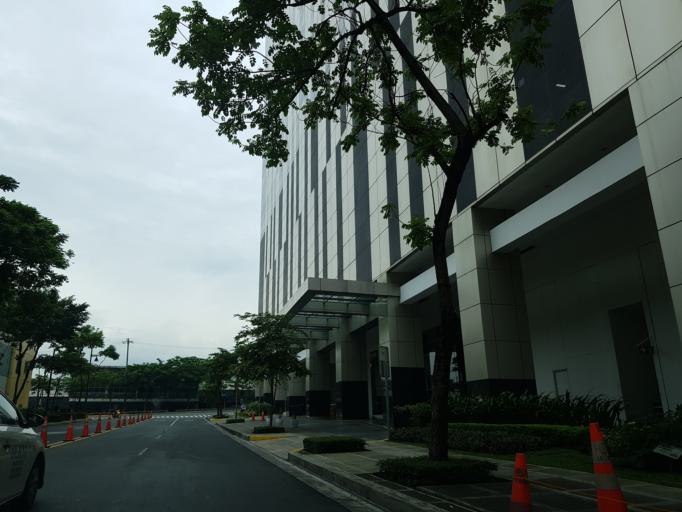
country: PH
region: Metro Manila
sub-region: Makati City
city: Makati City
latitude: 14.5545
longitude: 121.0449
